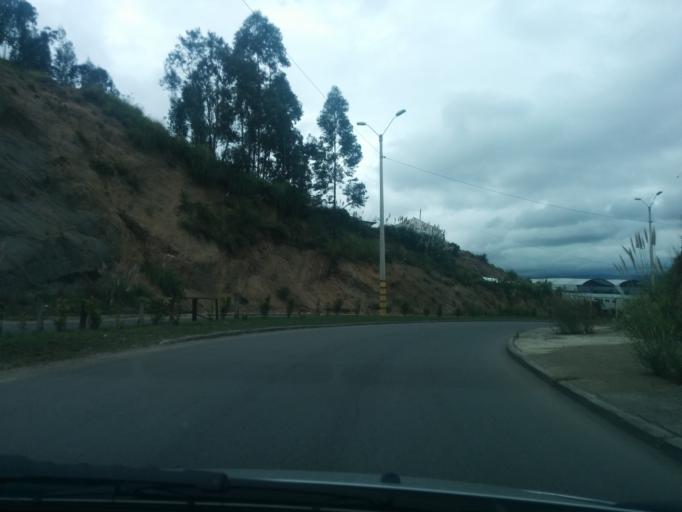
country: EC
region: Azuay
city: Cuenca
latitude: -2.8951
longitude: -78.9601
